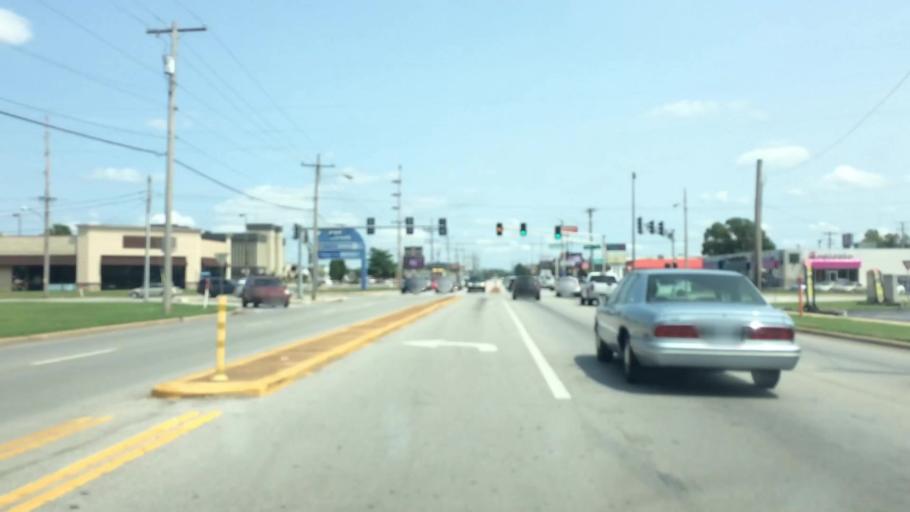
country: US
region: Missouri
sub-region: Greene County
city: Springfield
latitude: 37.1595
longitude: -93.2726
